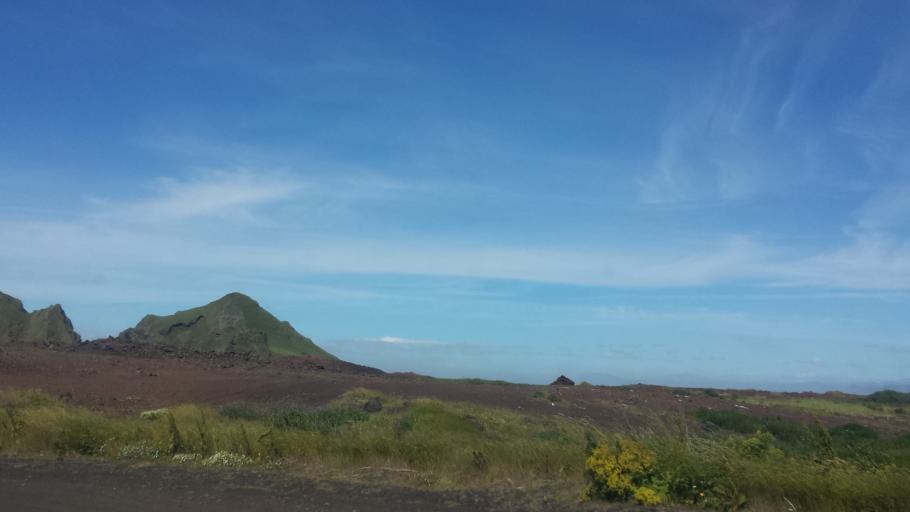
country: IS
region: South
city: Vestmannaeyjar
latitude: 63.4393
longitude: -20.2450
